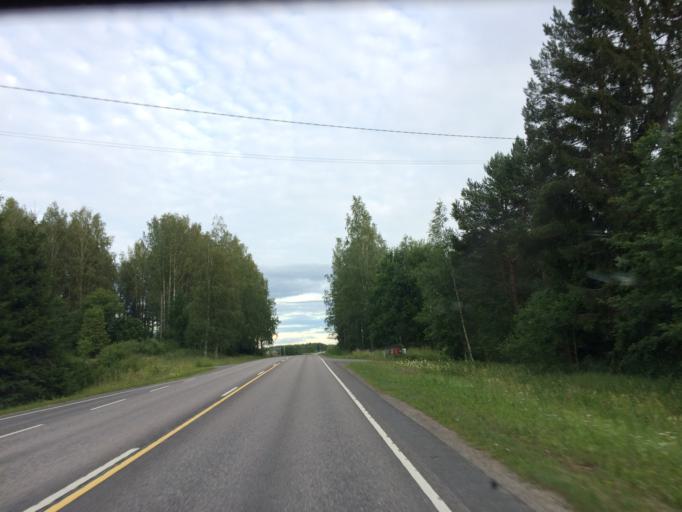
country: FI
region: Haeme
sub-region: Haemeenlinna
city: Tervakoski
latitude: 60.8398
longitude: 24.6191
